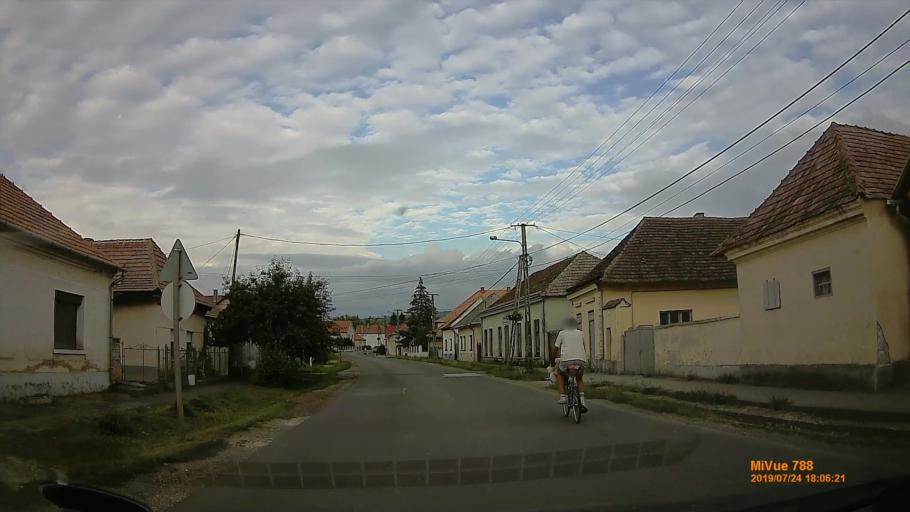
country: HU
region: Borsod-Abauj-Zemplen
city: Abaujszanto
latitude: 48.2840
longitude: 21.1824
